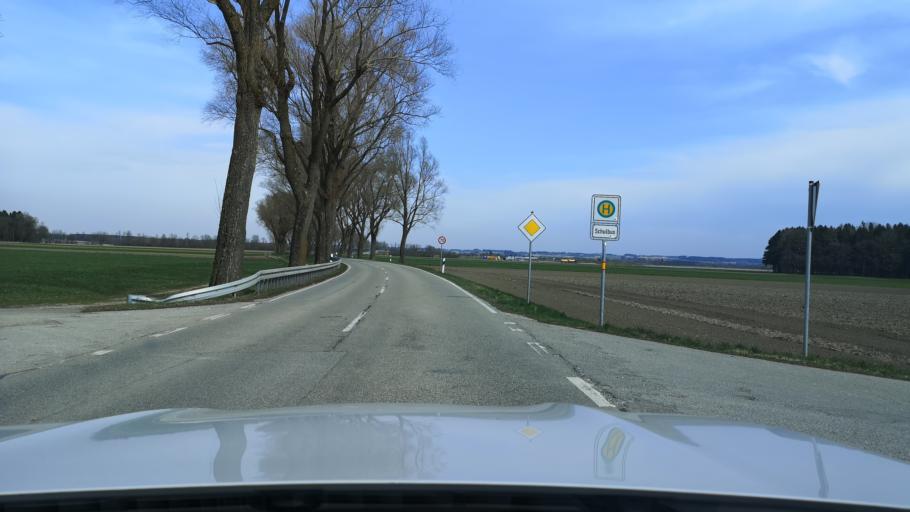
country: DE
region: Bavaria
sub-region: Upper Bavaria
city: Forstinning
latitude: 48.1955
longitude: 11.9139
